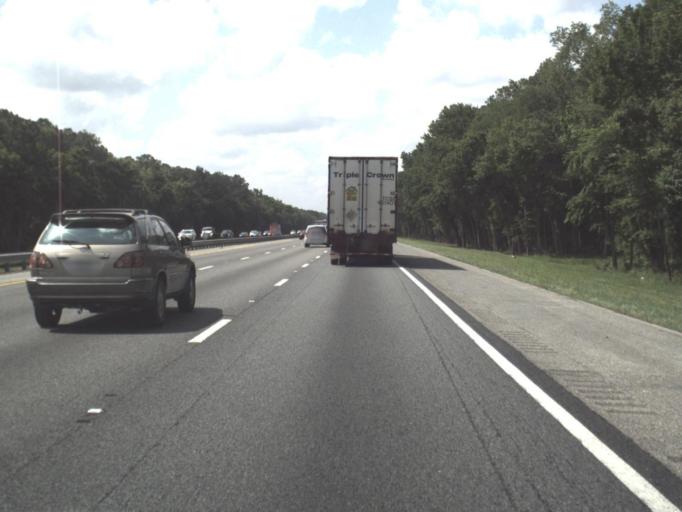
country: US
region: Florida
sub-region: Saint Johns County
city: Fruit Cove
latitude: 30.0207
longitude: -81.4825
